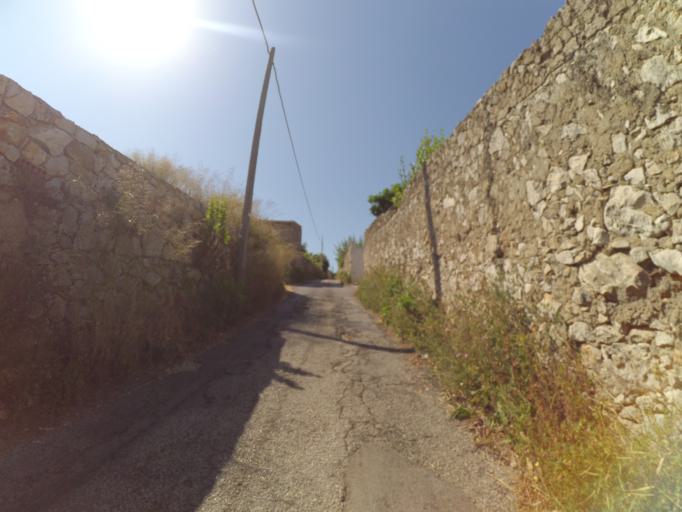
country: IT
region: Latium
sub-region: Provincia di Latina
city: Gaeta
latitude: 41.2191
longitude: 13.5505
